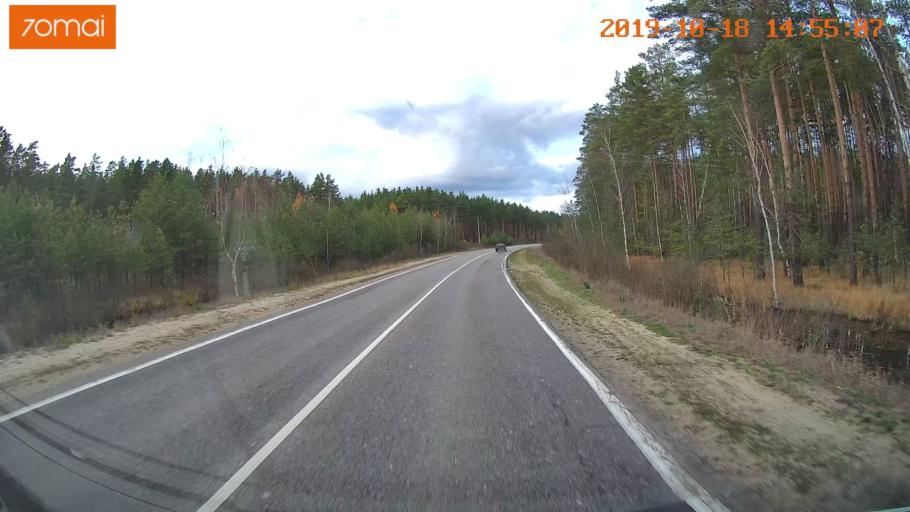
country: RU
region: Vladimir
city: Kurlovo
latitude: 55.4475
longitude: 40.5892
